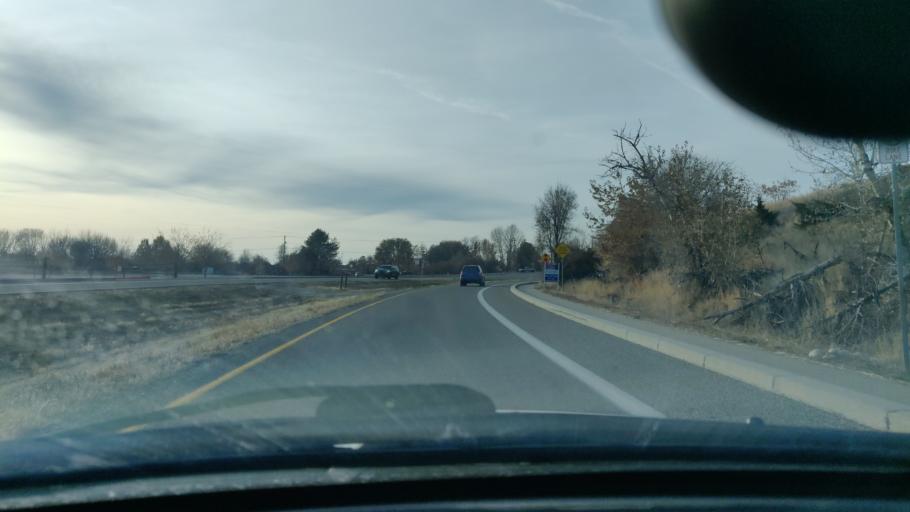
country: US
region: Idaho
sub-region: Ada County
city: Eagle
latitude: 43.6915
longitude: -116.3109
